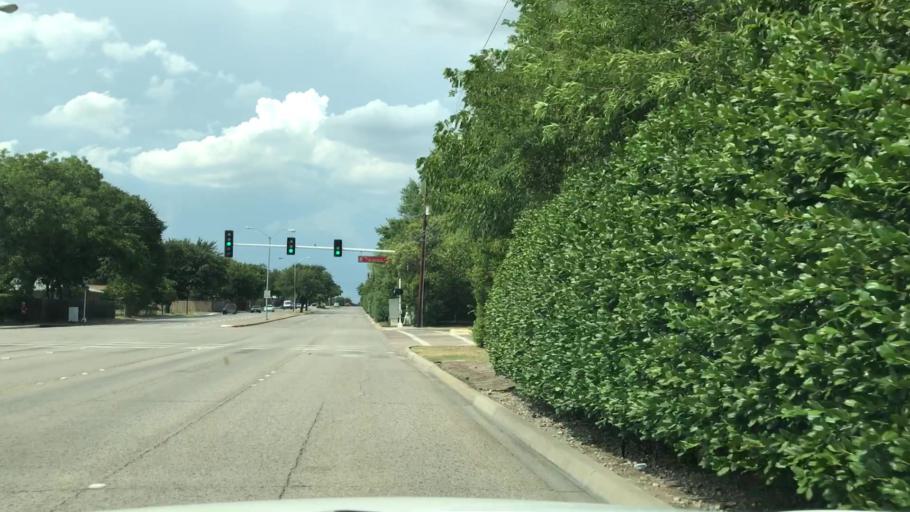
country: US
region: Texas
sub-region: Dallas County
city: Carrollton
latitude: 32.9384
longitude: -96.8731
